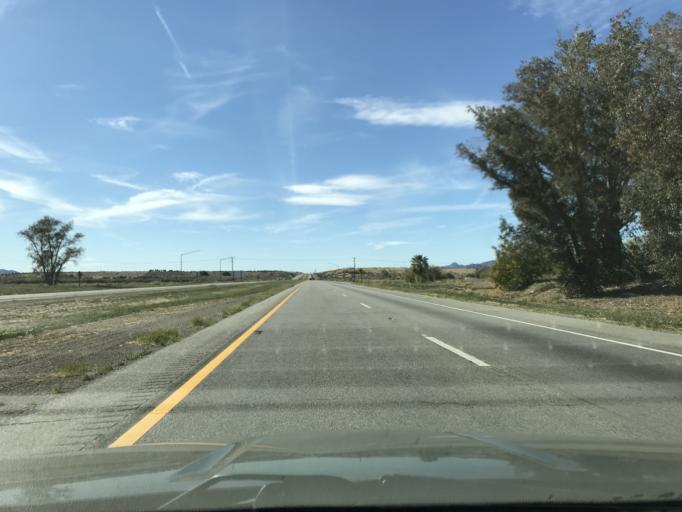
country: US
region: California
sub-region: Riverside County
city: Blythe
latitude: 33.6070
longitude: -114.6593
